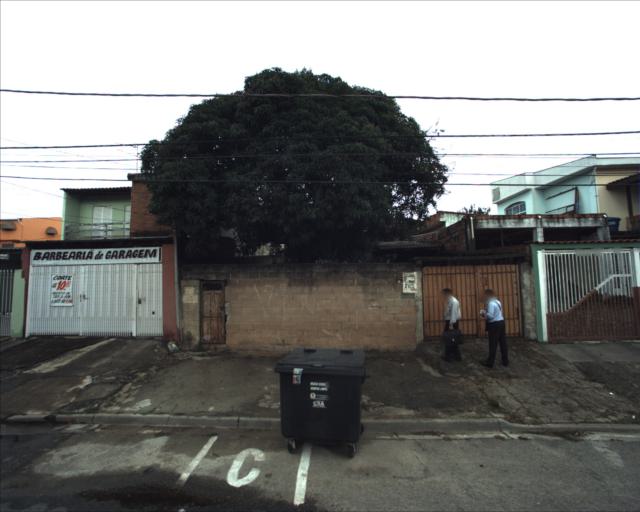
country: BR
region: Sao Paulo
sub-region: Sorocaba
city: Sorocaba
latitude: -23.5049
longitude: -47.5010
